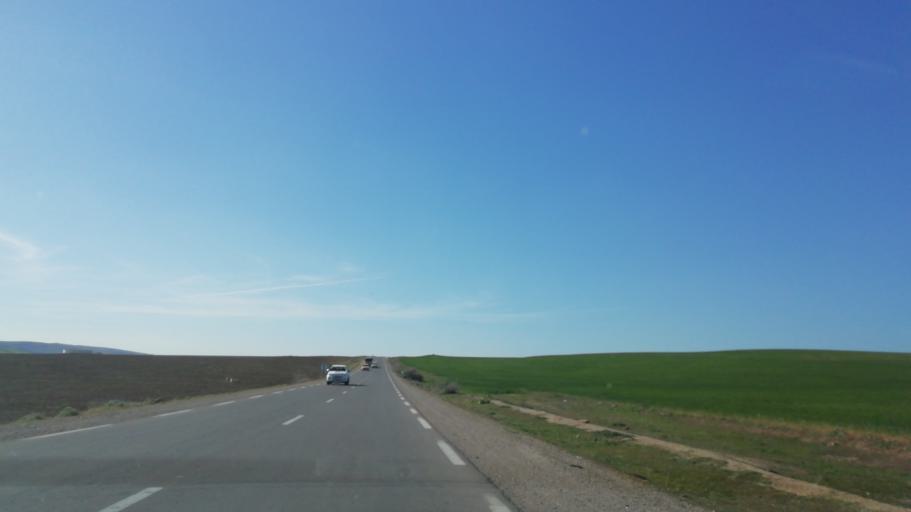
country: DZ
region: Mascara
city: Oued el Abtal
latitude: 35.4466
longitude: 0.8190
